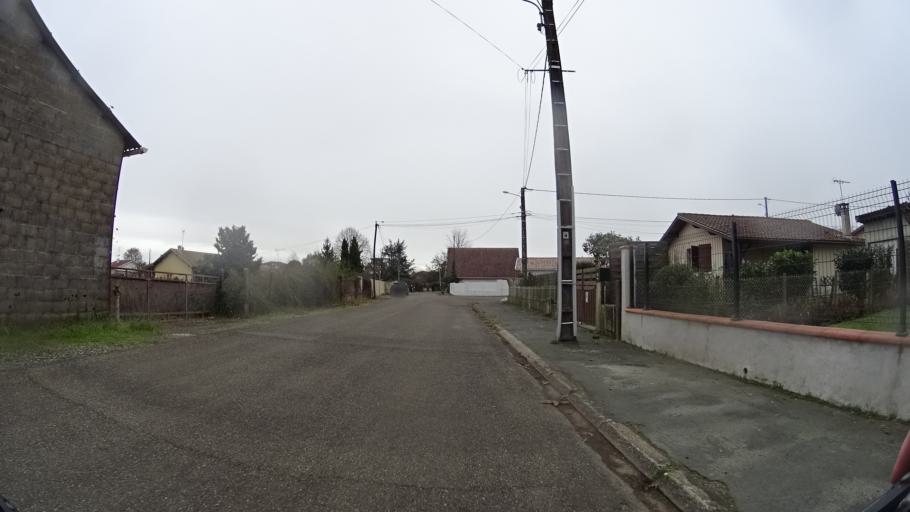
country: FR
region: Aquitaine
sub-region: Departement des Landes
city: Saint-Paul-les-Dax
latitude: 43.7325
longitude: -1.0511
